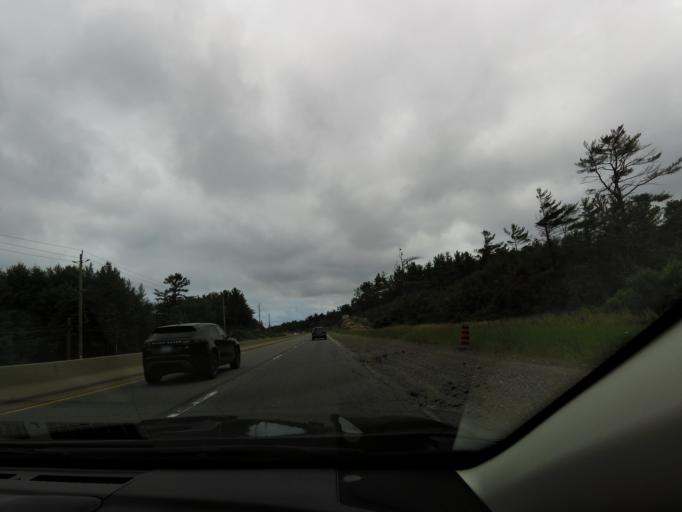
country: CA
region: Ontario
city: Gravenhurst
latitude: 44.8695
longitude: -79.3260
